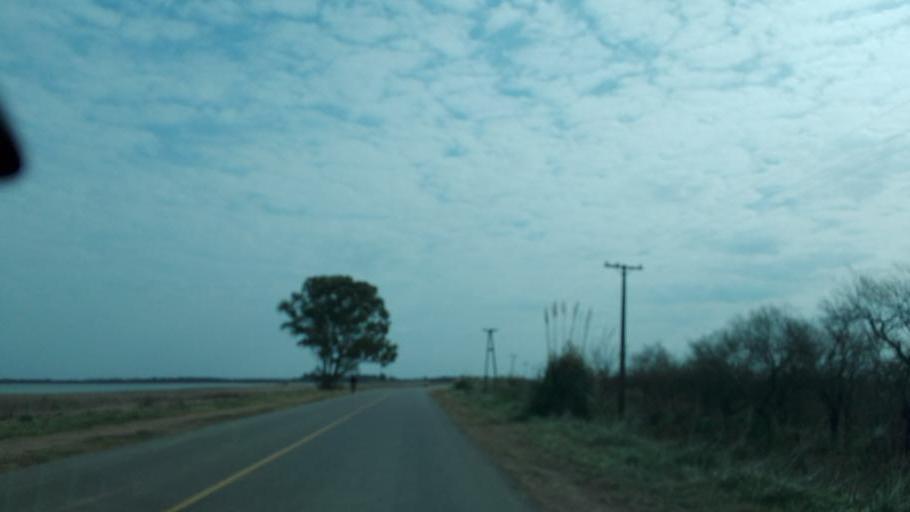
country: AR
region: Buenos Aires
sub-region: Partido de Chascomus
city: Chascomus
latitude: -35.5614
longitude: -58.0364
